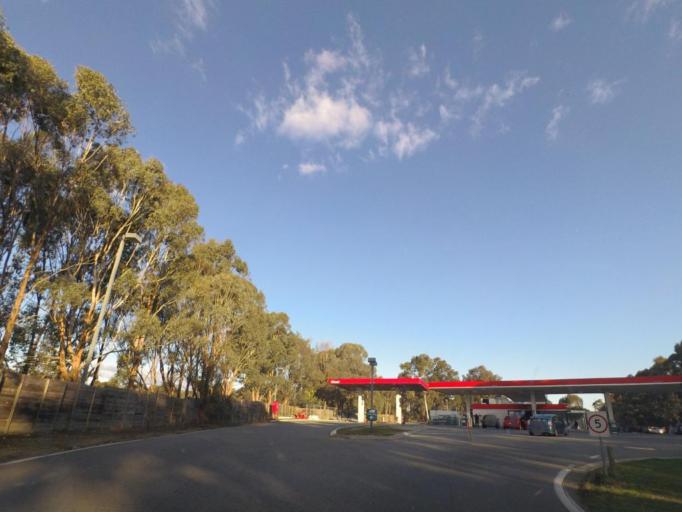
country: AU
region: Victoria
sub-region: Murrindindi
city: Kinglake West
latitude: -37.0626
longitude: 145.1019
